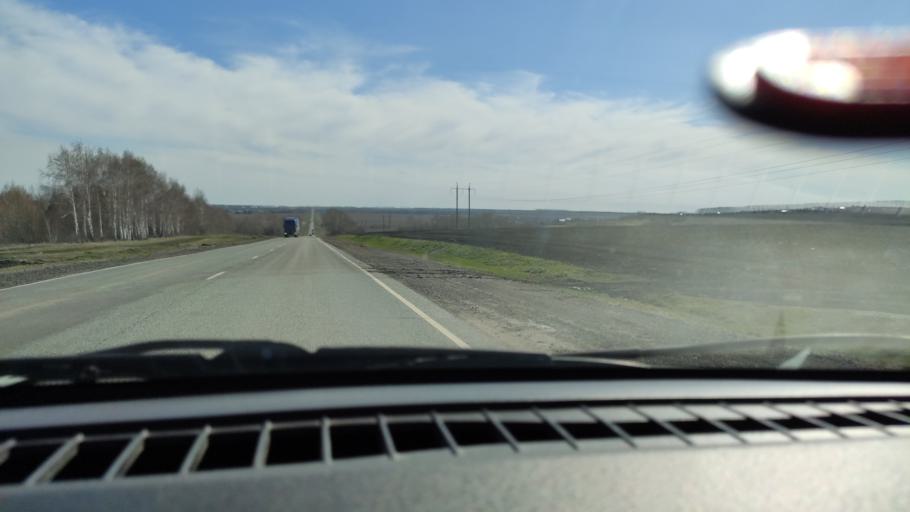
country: RU
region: Bashkortostan
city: Sterlitamak
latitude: 53.6897
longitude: 55.8609
